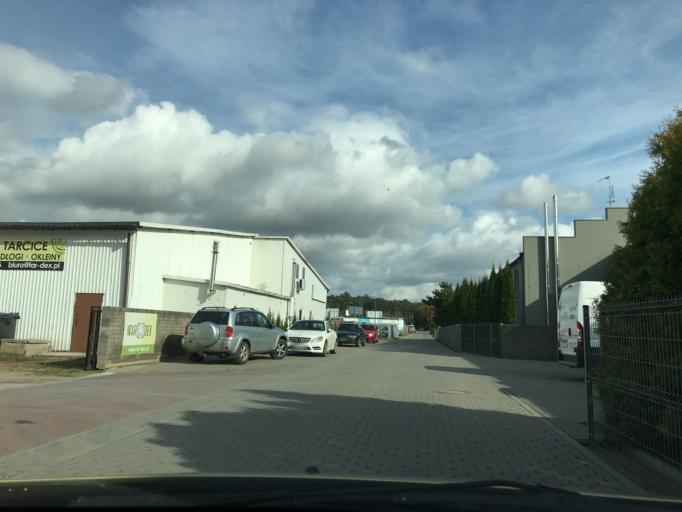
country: PL
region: Greater Poland Voivodeship
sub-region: Powiat poznanski
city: Baranowo
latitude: 52.4136
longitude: 16.7864
